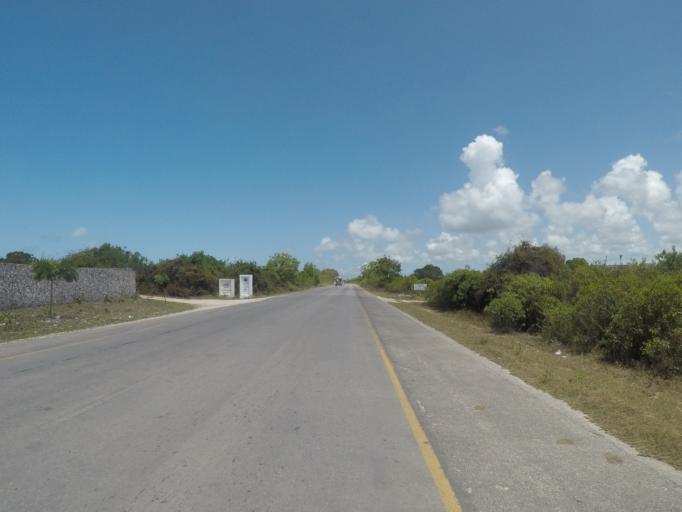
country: TZ
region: Zanzibar Central/South
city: Nganane
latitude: -6.3016
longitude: 39.5386
